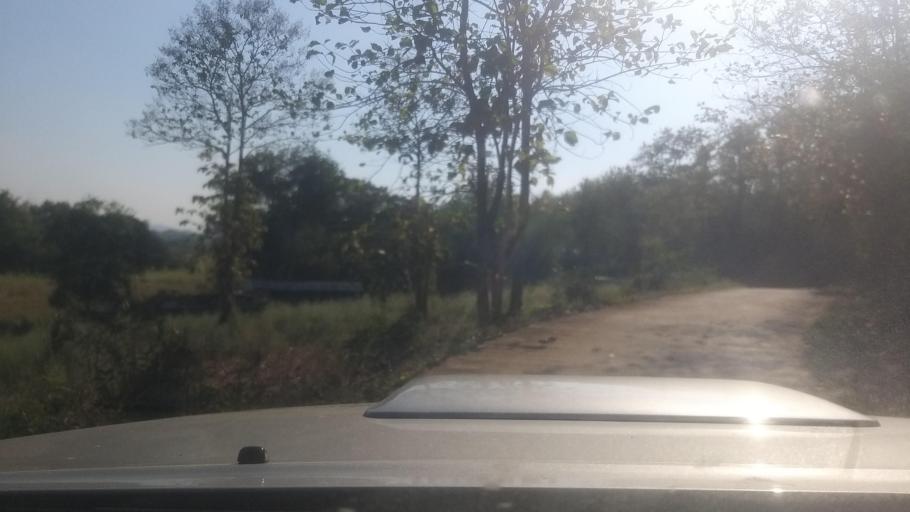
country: TH
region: Phrae
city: Phrae
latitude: 18.2752
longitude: 99.9899
